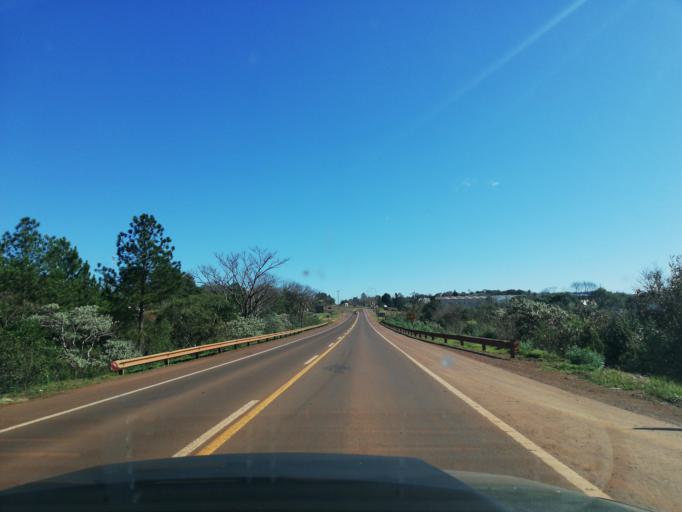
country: AR
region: Misiones
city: Aristobulo del Valle
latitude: -27.0997
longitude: -54.8809
